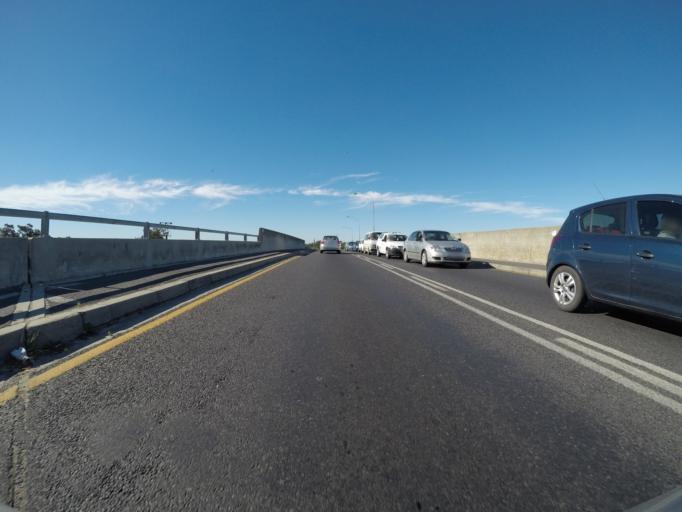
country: ZA
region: Western Cape
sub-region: City of Cape Town
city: Kraaifontein
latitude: -33.9321
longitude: 18.6761
